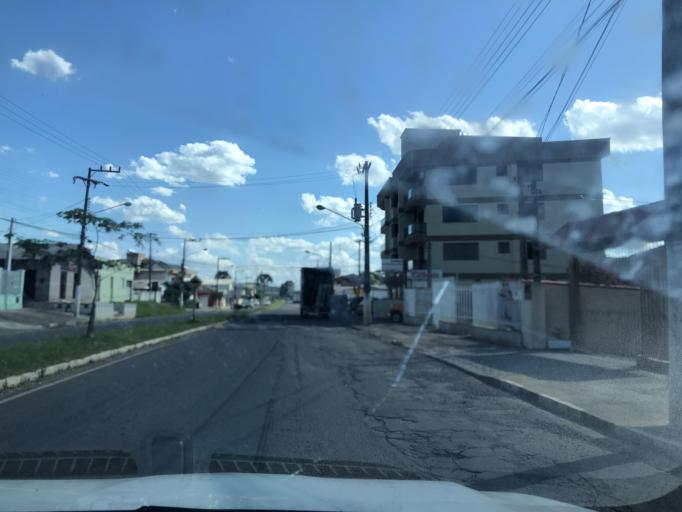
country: BR
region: Santa Catarina
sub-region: Lages
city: Lages
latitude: -27.8185
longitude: -50.3056
